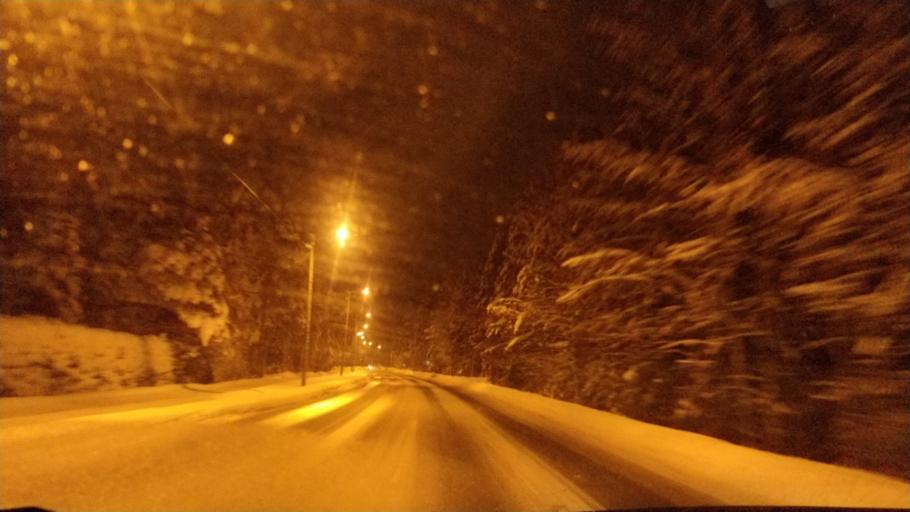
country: FI
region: Lapland
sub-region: Rovaniemi
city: Rovaniemi
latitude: 66.3795
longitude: 25.3801
